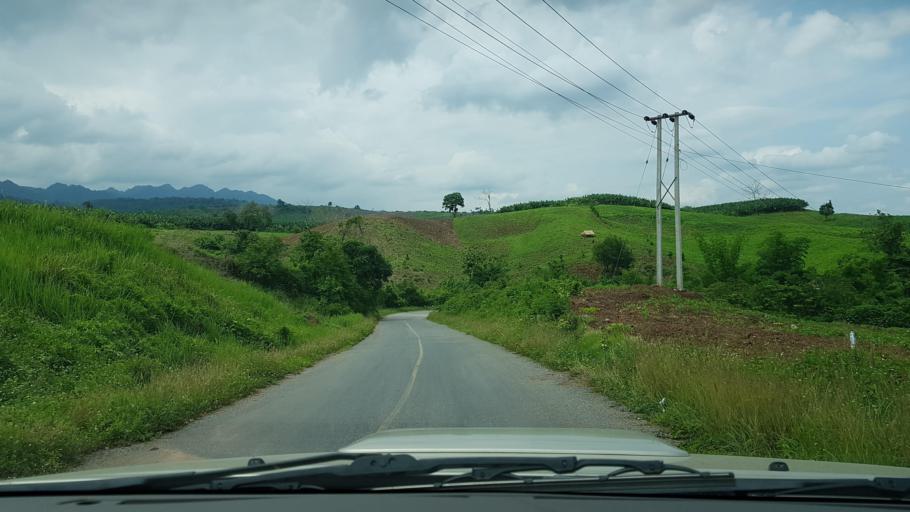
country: TH
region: Nan
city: Chaloem Phra Kiat
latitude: 20.0181
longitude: 101.3212
